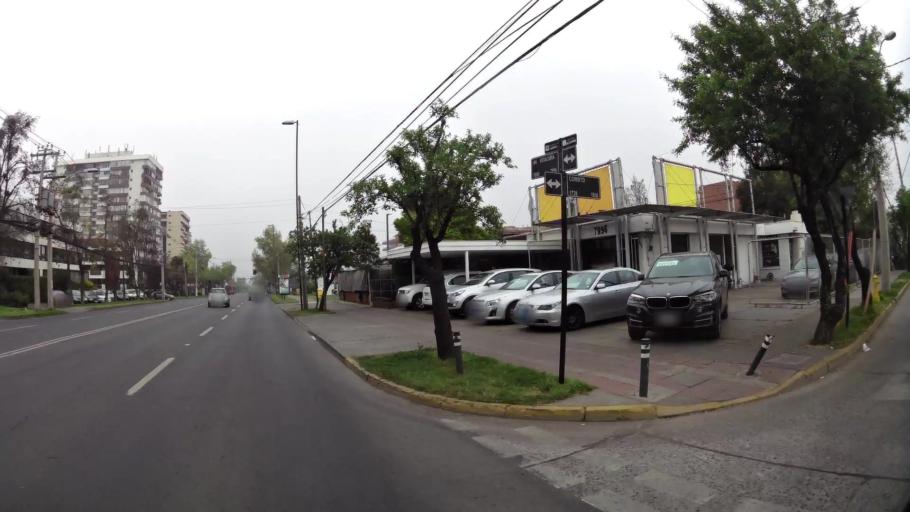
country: CL
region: Santiago Metropolitan
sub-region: Provincia de Santiago
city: Villa Presidente Frei, Nunoa, Santiago, Chile
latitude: -33.3855
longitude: -70.5574
